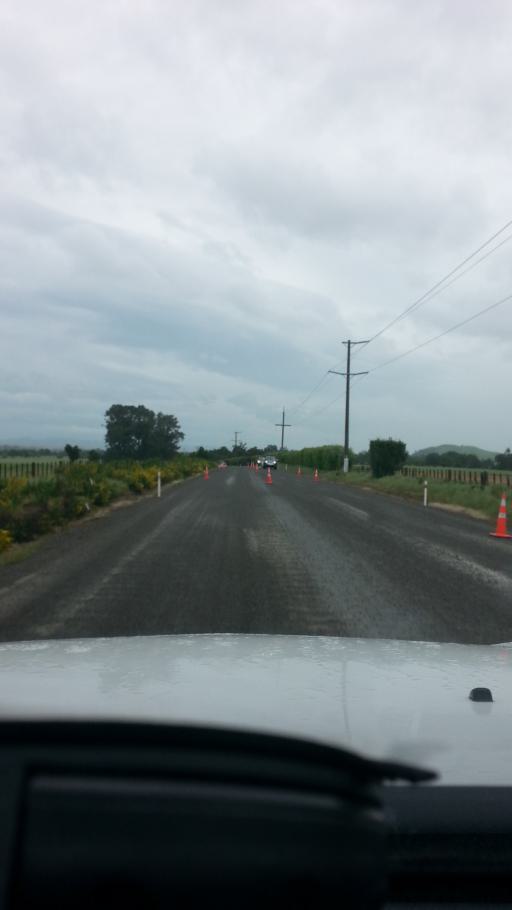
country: NZ
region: Wellington
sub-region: Masterton District
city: Masterton
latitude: -40.8222
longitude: 175.6244
